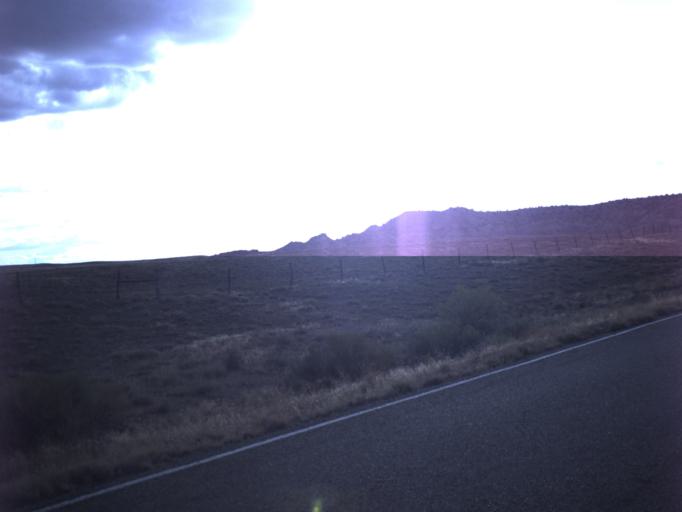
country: US
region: Utah
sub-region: San Juan County
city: Blanding
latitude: 37.4218
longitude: -109.4636
